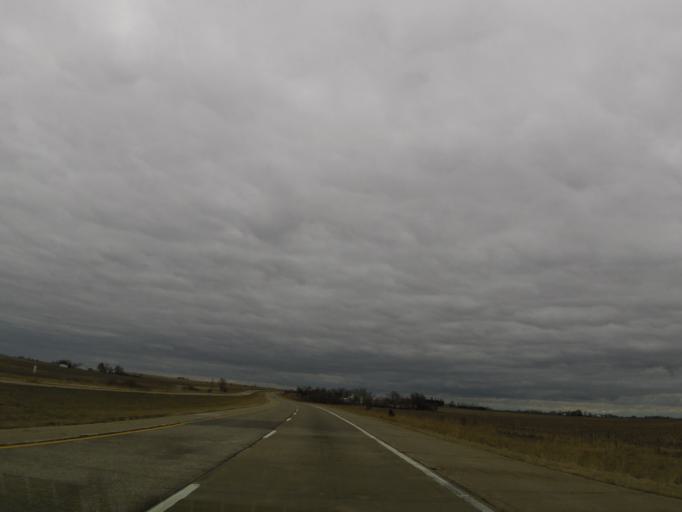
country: US
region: Iowa
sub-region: Benton County
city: Urbana
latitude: 42.2805
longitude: -91.9393
